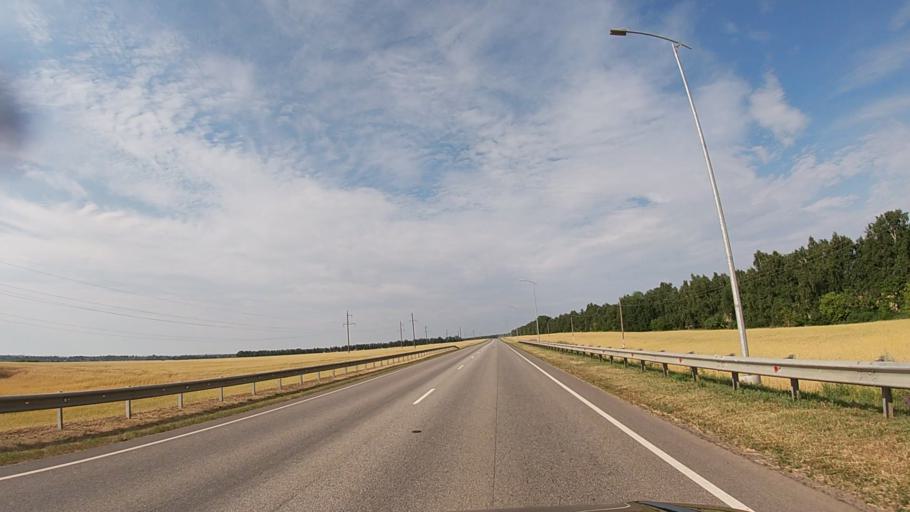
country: RU
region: Belgorod
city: Proletarskiy
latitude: 50.8213
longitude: 35.7574
